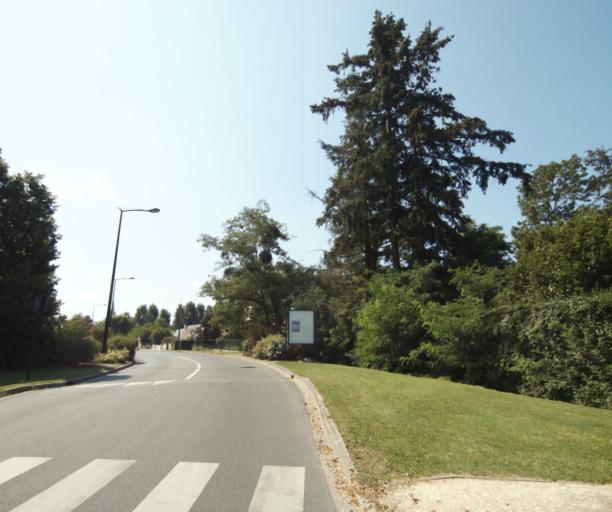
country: FR
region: Centre
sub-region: Departement du Loiret
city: Saint-Cyr-en-Val
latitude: 47.8349
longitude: 1.9669
